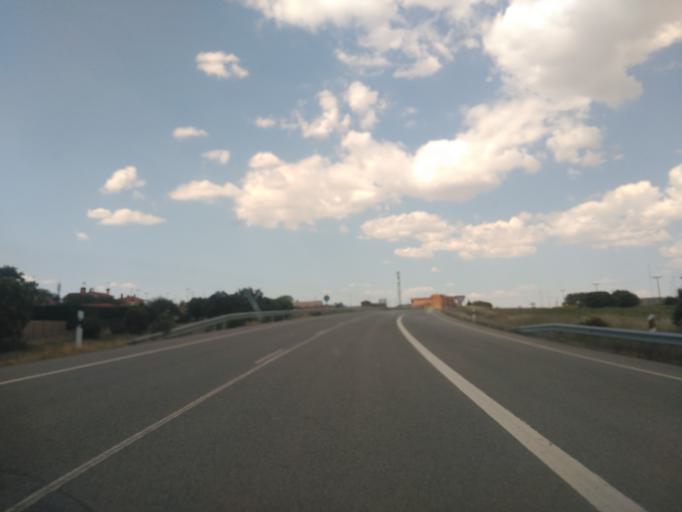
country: ES
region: Castille and Leon
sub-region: Provincia de Salamanca
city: Martinamor
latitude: 40.8074
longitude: -5.6325
